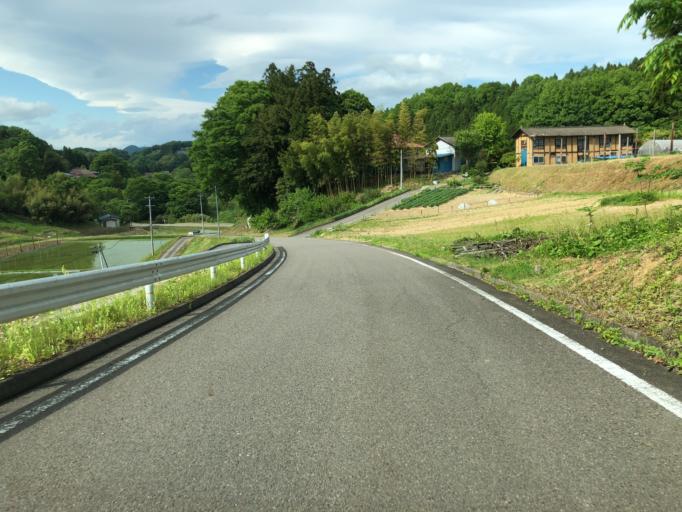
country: JP
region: Fukushima
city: Nihommatsu
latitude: 37.6180
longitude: 140.5319
